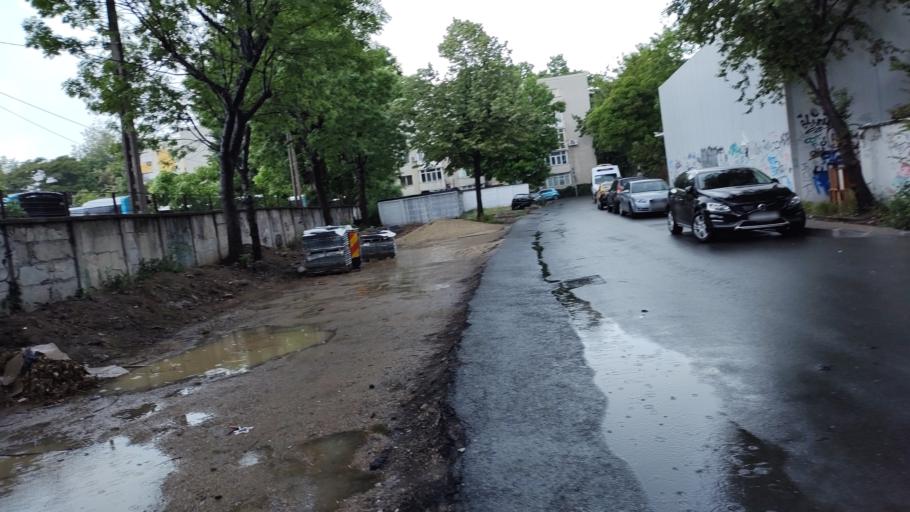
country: RO
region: Bucuresti
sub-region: Municipiul Bucuresti
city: Bucharest
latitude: 44.4612
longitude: 26.1045
